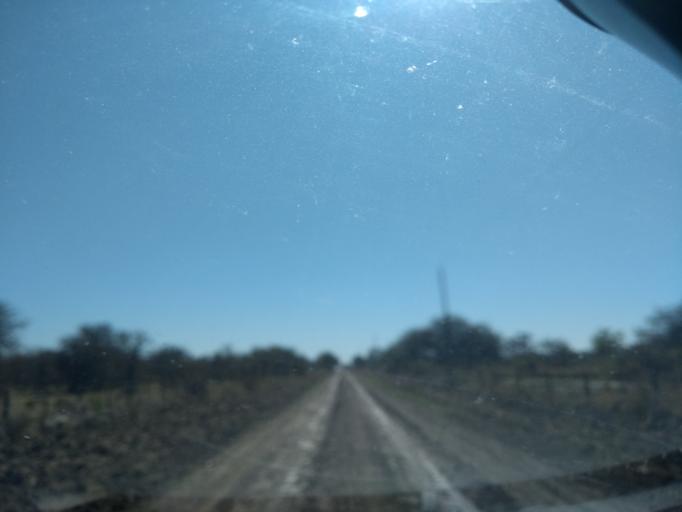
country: AR
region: Chaco
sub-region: Departamento de Quitilipi
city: Quitilipi
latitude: -26.7474
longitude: -60.2390
